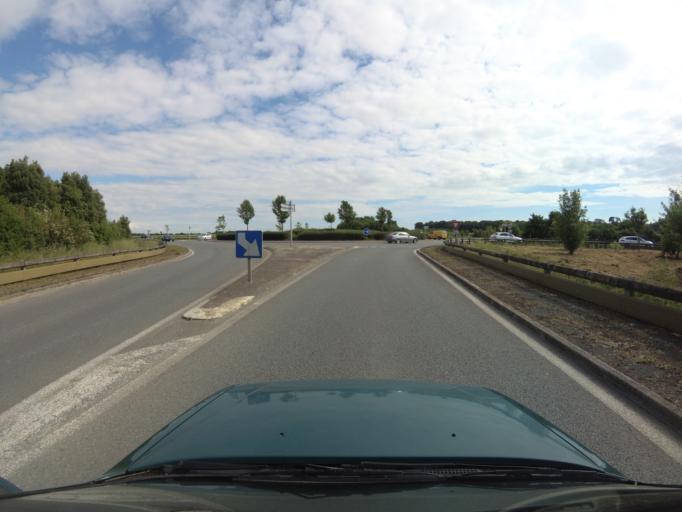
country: FR
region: Poitou-Charentes
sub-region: Departement de la Charente-Maritime
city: Saint-Xandre
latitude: 46.1958
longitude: -1.0953
